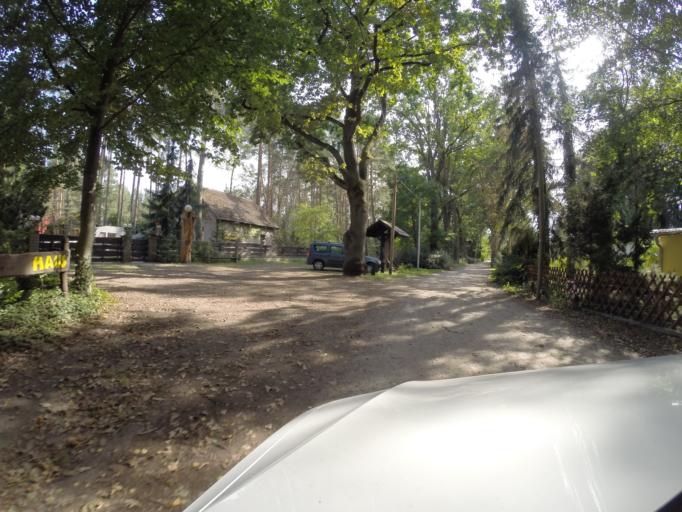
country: DE
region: Brandenburg
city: Baruth
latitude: 52.1201
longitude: 13.5281
